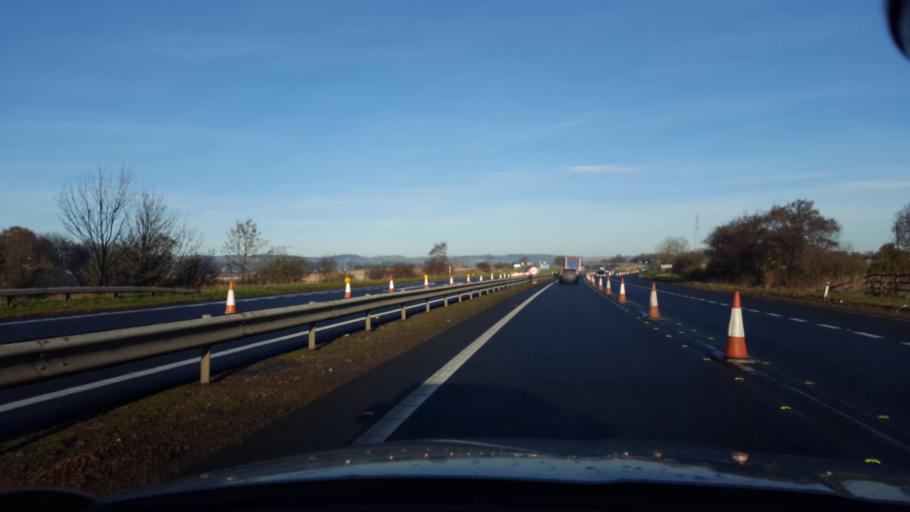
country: GB
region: Scotland
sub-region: Fife
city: Kelty
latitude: 56.1617
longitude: -3.4026
